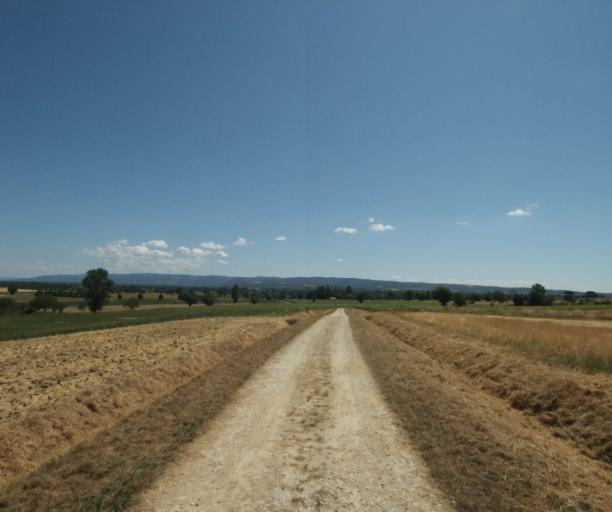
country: FR
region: Midi-Pyrenees
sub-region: Departement de la Haute-Garonne
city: Saint-Felix-Lauragais
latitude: 43.4709
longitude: 1.9217
